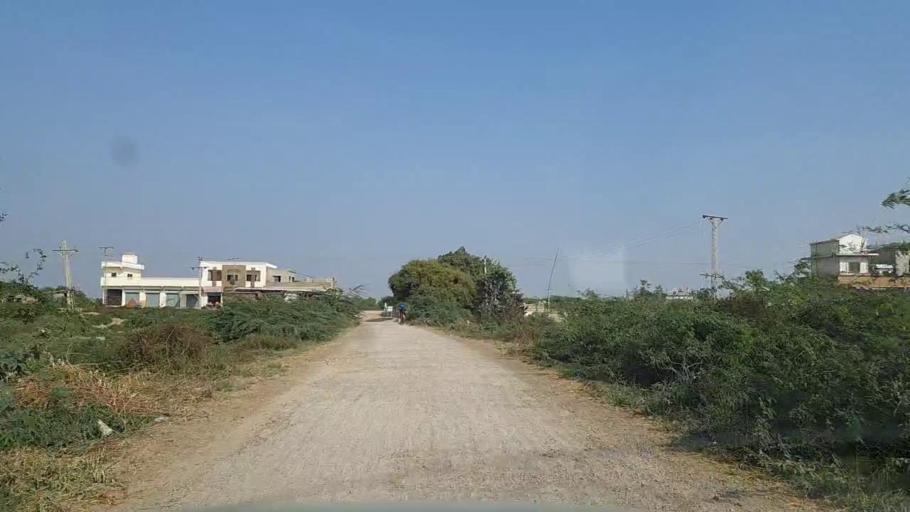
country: PK
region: Sindh
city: Mirpur Sakro
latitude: 24.5655
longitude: 67.6210
